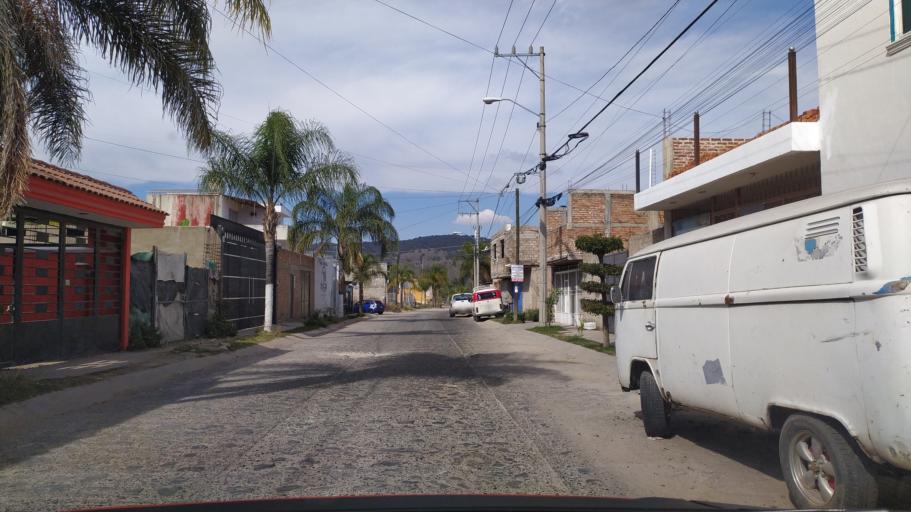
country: MX
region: Jalisco
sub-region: Tlajomulco de Zuniga
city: Palomar
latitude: 20.6291
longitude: -103.4738
